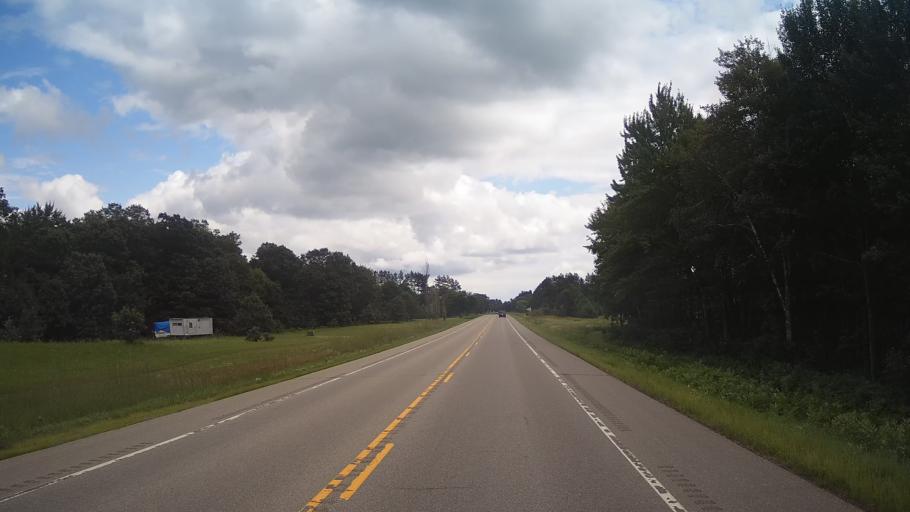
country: US
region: Wisconsin
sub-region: Adams County
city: Friendship
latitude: 44.0240
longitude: -89.6728
